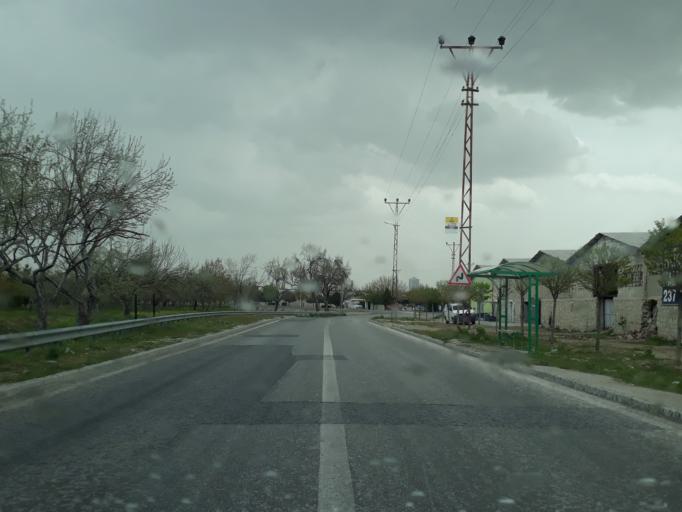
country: TR
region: Konya
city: Selcuklu
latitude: 37.9175
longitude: 32.4745
